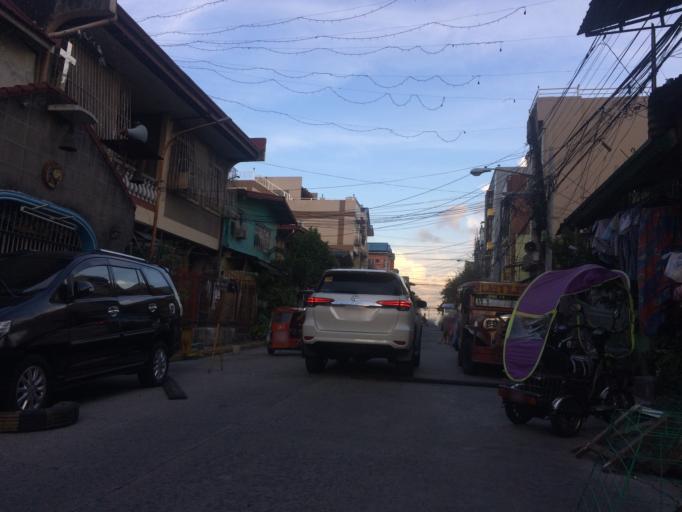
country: PH
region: Metro Manila
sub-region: City of Manila
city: Manila
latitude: 14.6110
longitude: 121.0077
